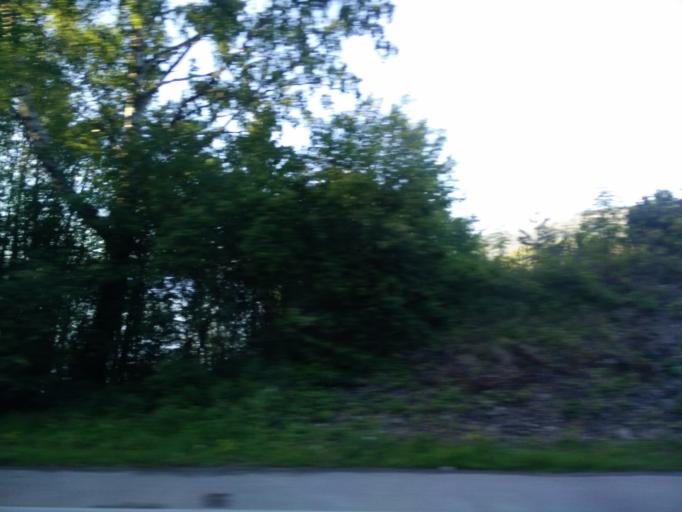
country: NO
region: Buskerud
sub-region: Hole
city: Vik
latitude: 60.0763
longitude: 10.2939
